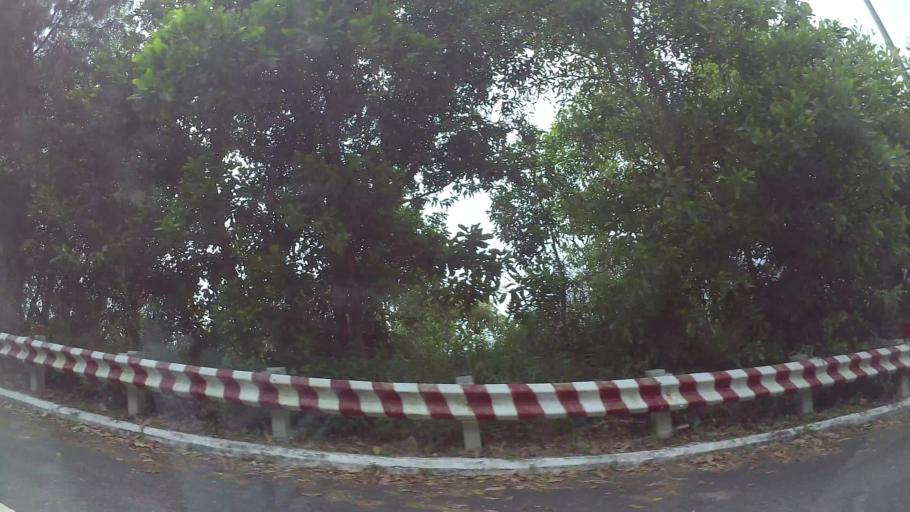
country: VN
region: Da Nang
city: Son Tra
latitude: 16.1000
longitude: 108.3038
